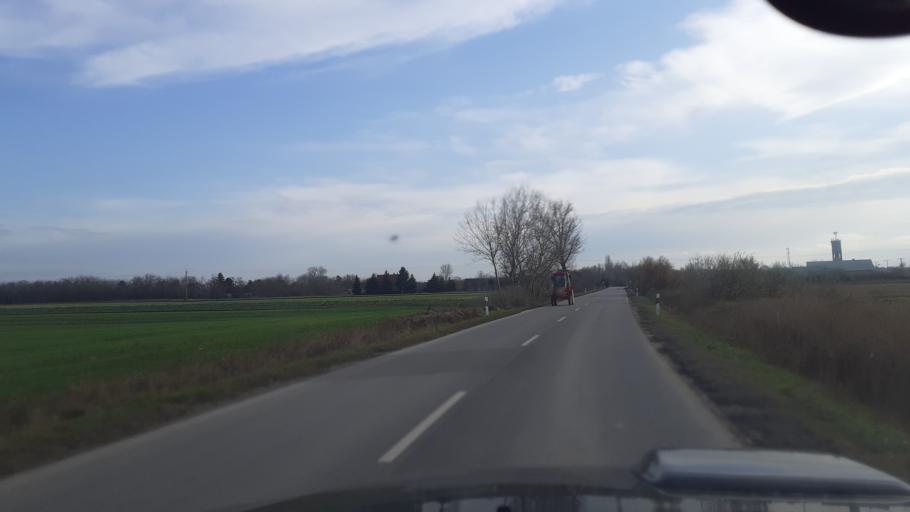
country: HU
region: Bacs-Kiskun
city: Kunszentmiklos
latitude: 47.0422
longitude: 19.1232
